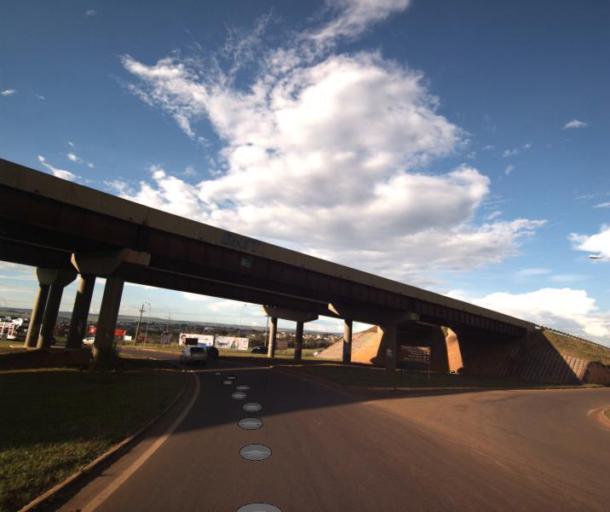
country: BR
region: Goias
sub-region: Anapolis
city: Anapolis
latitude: -16.3543
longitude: -48.9287
